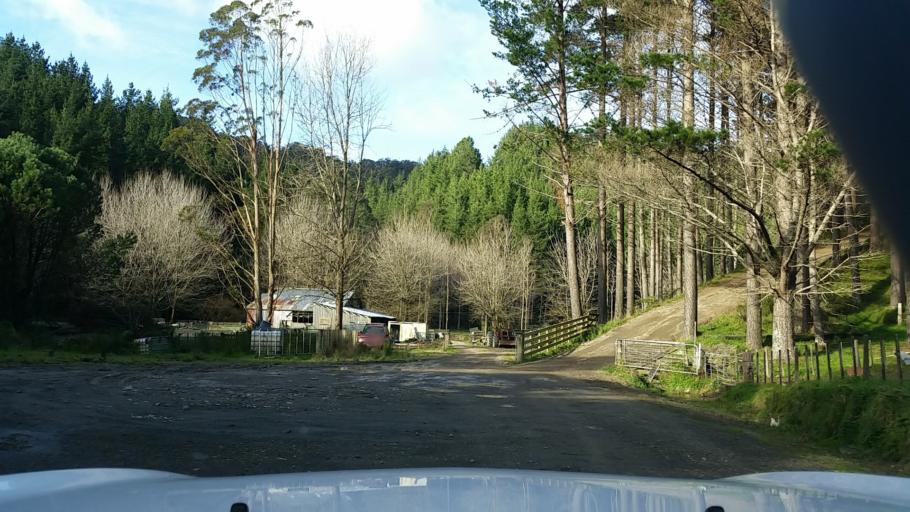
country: NZ
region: Taranaki
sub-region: New Plymouth District
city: Waitara
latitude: -38.9837
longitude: 174.4906
